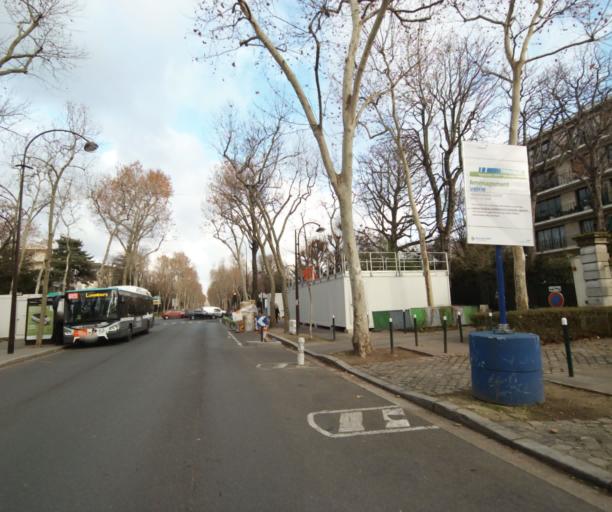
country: FR
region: Ile-de-France
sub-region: Departement des Hauts-de-Seine
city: Neuilly-sur-Seine
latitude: 48.8904
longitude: 2.2697
